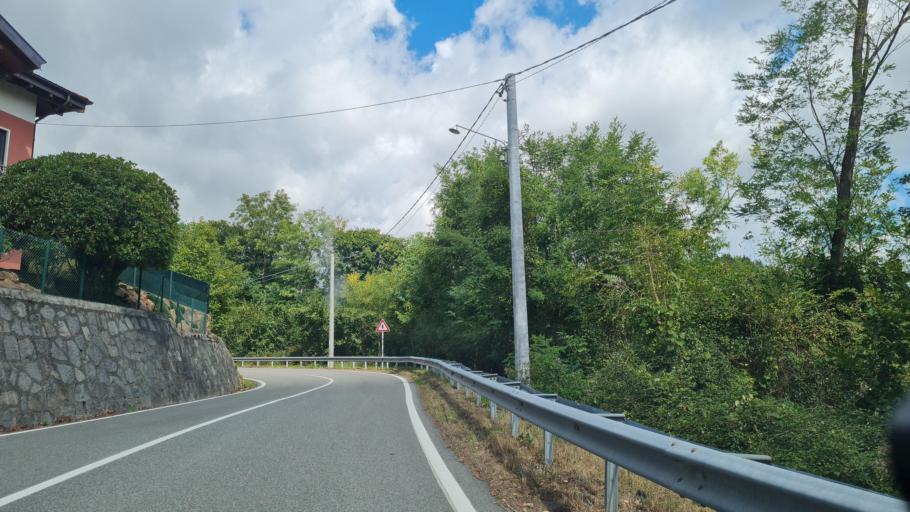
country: IT
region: Piedmont
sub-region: Provincia di Biella
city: Fontanella-Ozino
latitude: 45.6248
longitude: 8.1671
